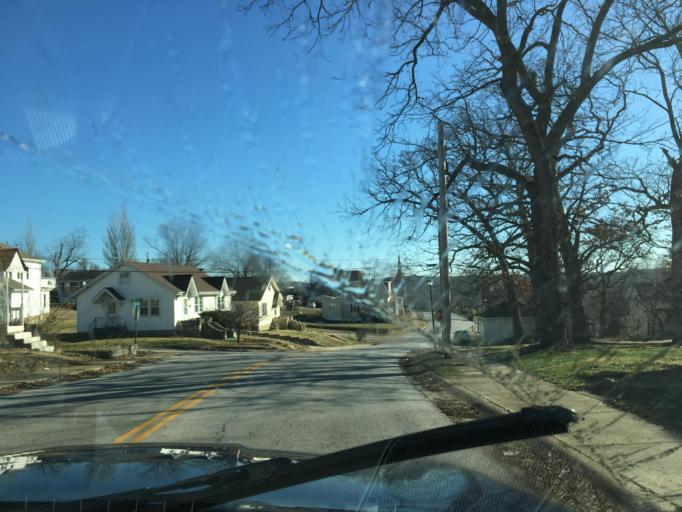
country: US
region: Missouri
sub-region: Jefferson County
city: De Soto
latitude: 38.1356
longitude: -90.5609
